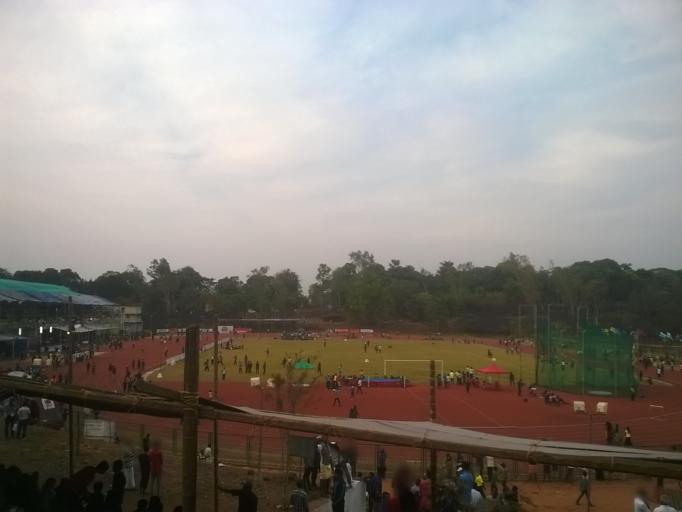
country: IN
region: Kerala
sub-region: Kozhikode
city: Kunnamangalam
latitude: 11.2790
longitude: 75.8373
